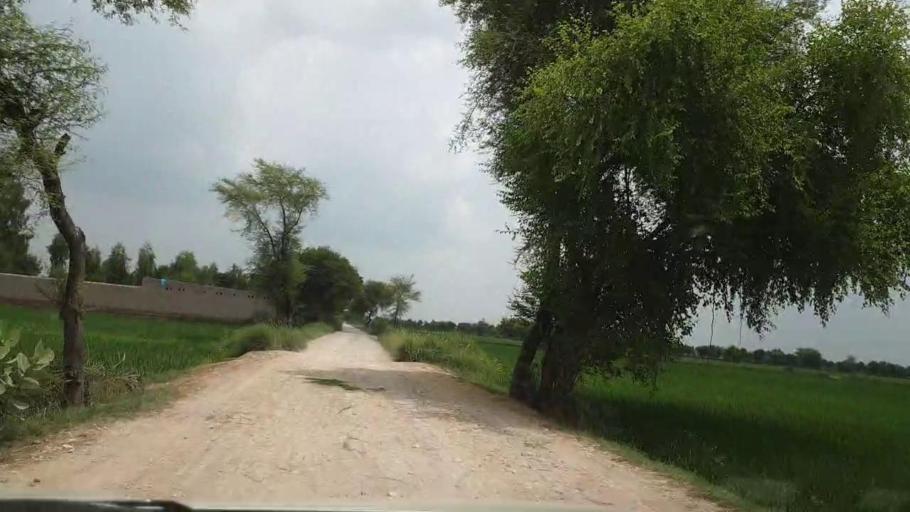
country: PK
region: Sindh
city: Goth Garelo
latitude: 27.4268
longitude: 68.0825
